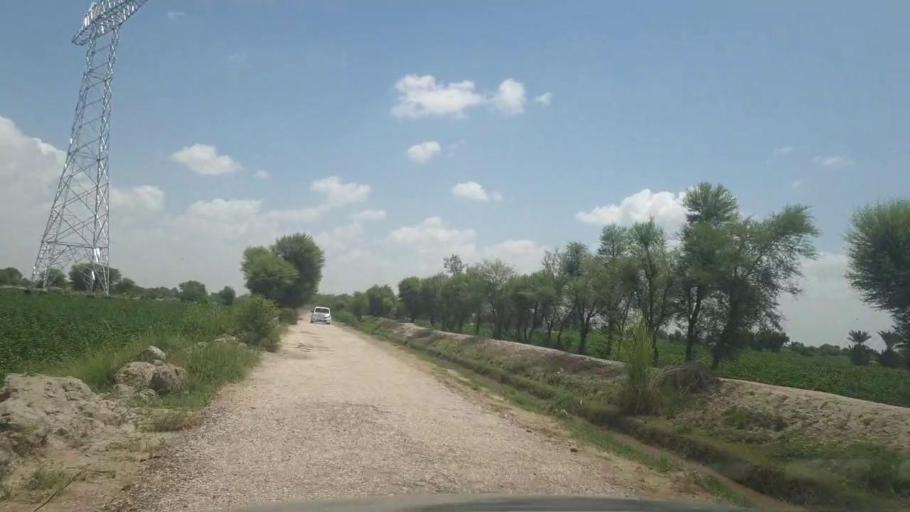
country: PK
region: Sindh
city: Kot Diji
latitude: 27.2582
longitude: 69.0470
